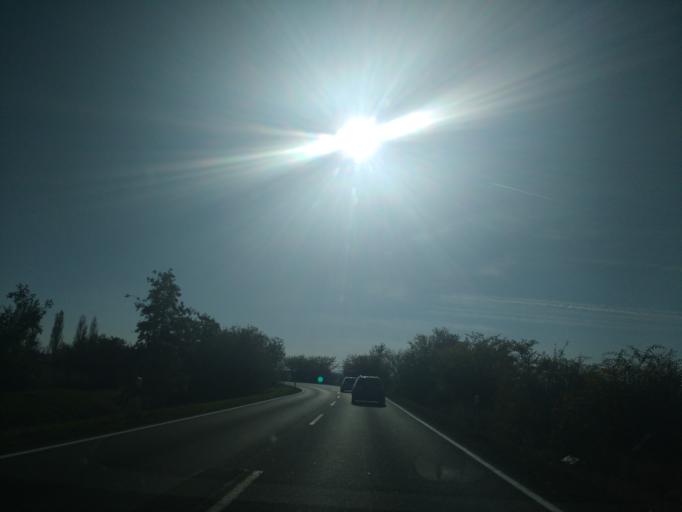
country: DE
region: Saxony-Anhalt
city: Sangerhausen
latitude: 51.4618
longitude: 11.2640
